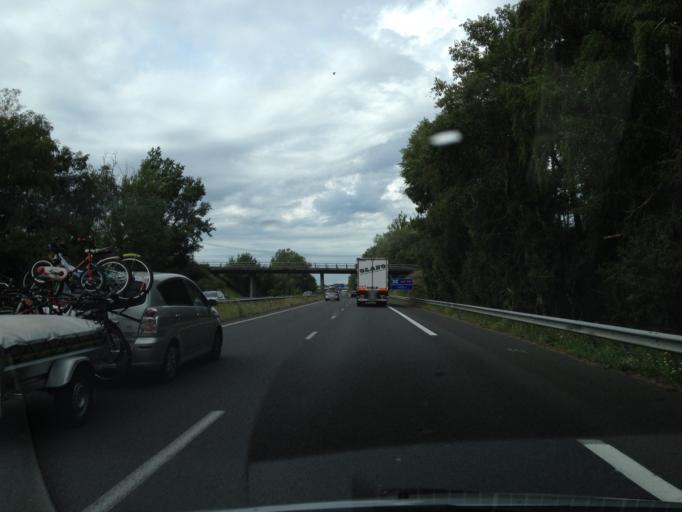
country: FR
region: Aquitaine
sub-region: Departement de la Gironde
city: Castets-en-Dorthe
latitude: 44.5317
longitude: -0.1812
